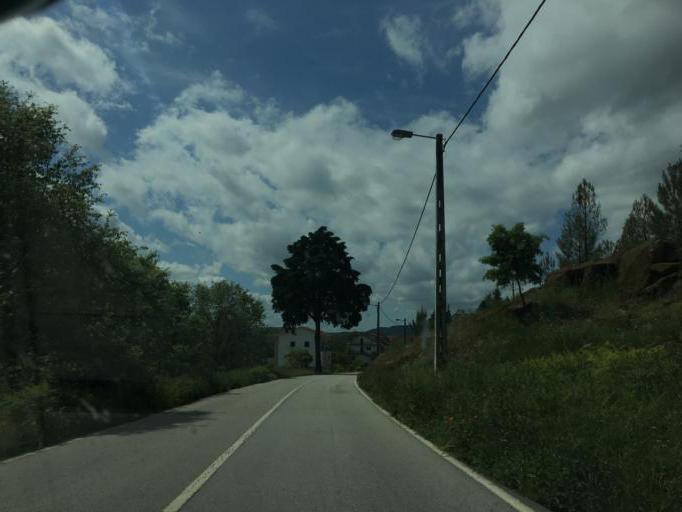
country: PT
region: Vila Real
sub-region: Boticas
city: Boticas
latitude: 41.7068
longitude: -7.6413
